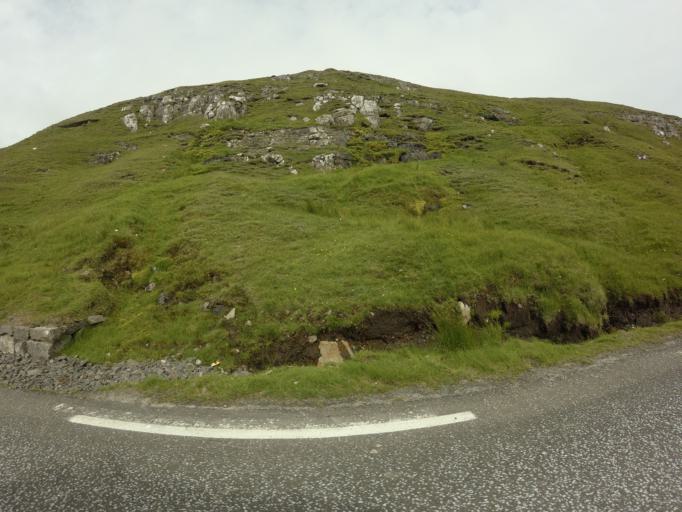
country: FO
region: Sandoy
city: Sandur
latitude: 61.8261
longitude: -6.7454
